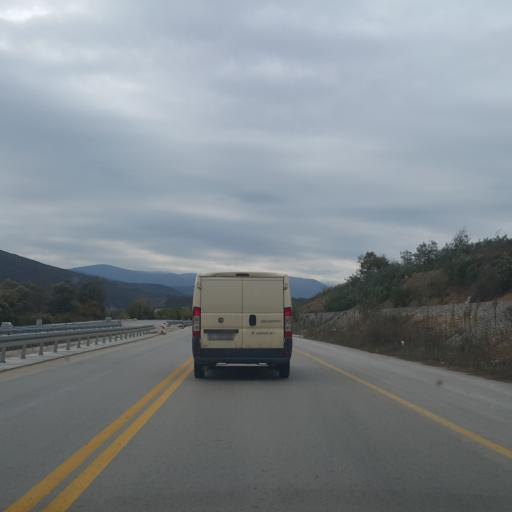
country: RS
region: Central Serbia
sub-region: Pirotski Okrug
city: Bela Palanka
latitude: 43.2327
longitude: 22.4478
